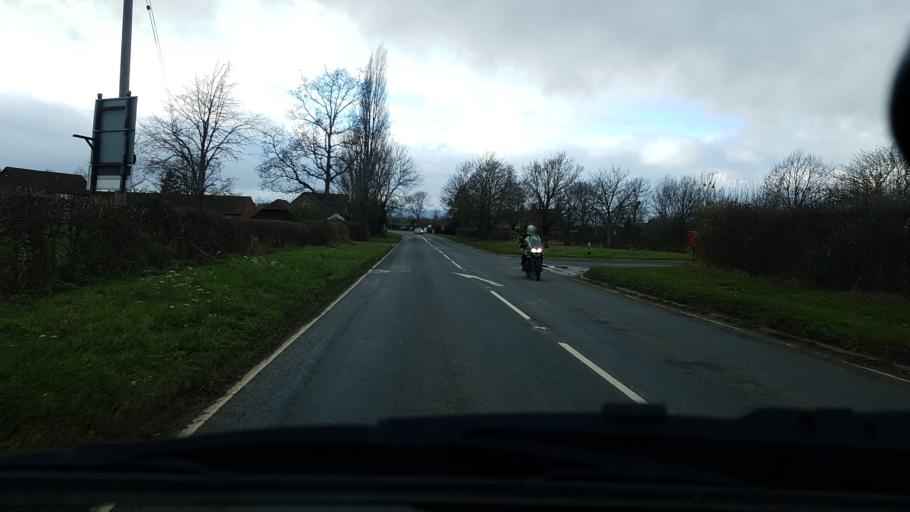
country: GB
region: England
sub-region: Worcestershire
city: Bredon
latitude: 52.0817
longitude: -2.1337
